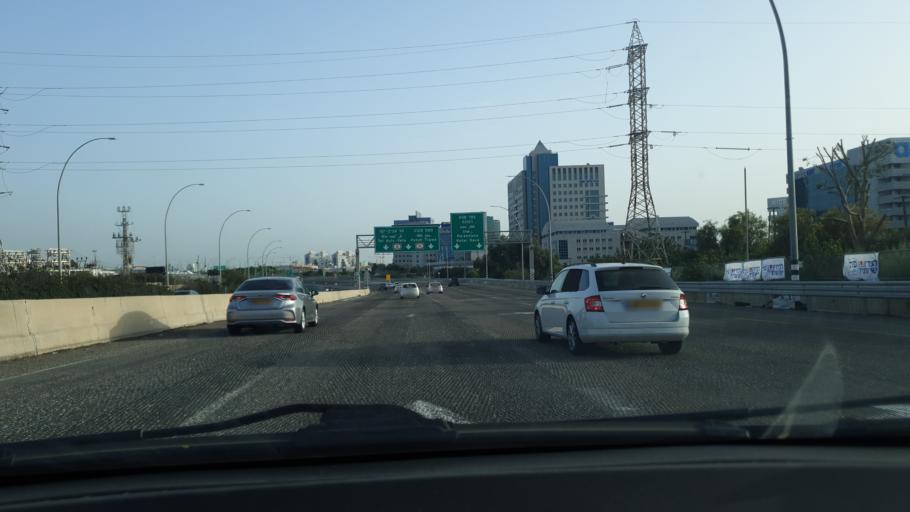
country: IL
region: Central District
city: Ra'anana
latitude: 32.2000
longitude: 34.8846
